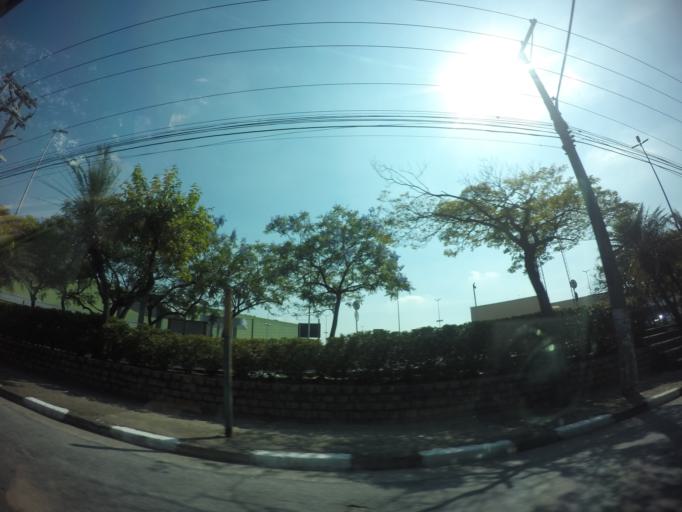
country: BR
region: Sao Paulo
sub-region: Sao Paulo
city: Sao Paulo
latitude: -23.5154
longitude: -46.6204
